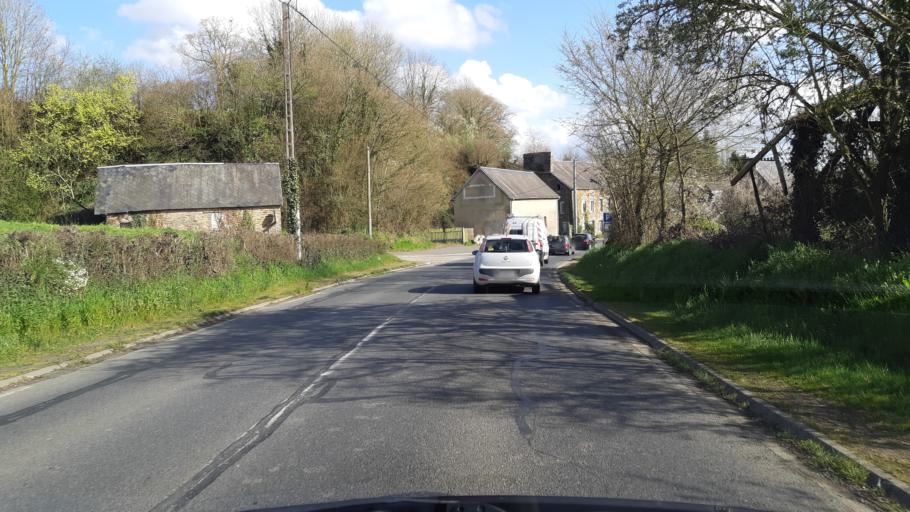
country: FR
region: Lower Normandy
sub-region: Departement de la Manche
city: Agneaux
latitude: 49.0934
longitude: -1.1180
